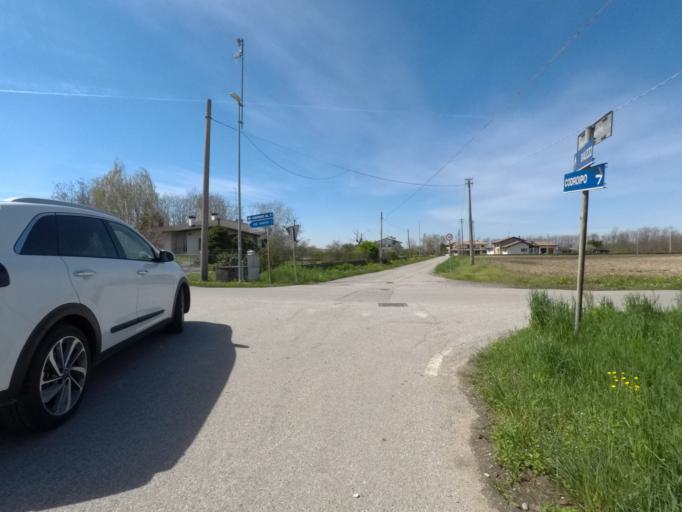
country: IT
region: Friuli Venezia Giulia
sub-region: Provincia di Udine
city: Camino al Tagliamento
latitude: 45.9494
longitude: 12.9396
